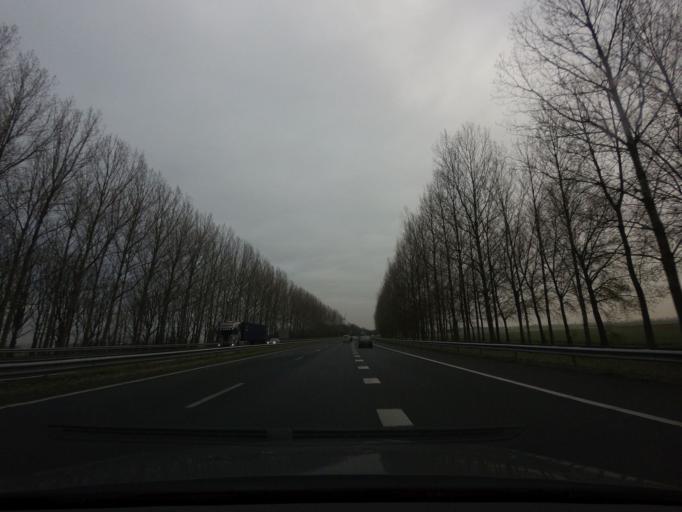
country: NL
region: North Holland
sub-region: Gemeente Medemblik
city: Opperdoes
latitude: 52.8106
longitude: 5.0105
